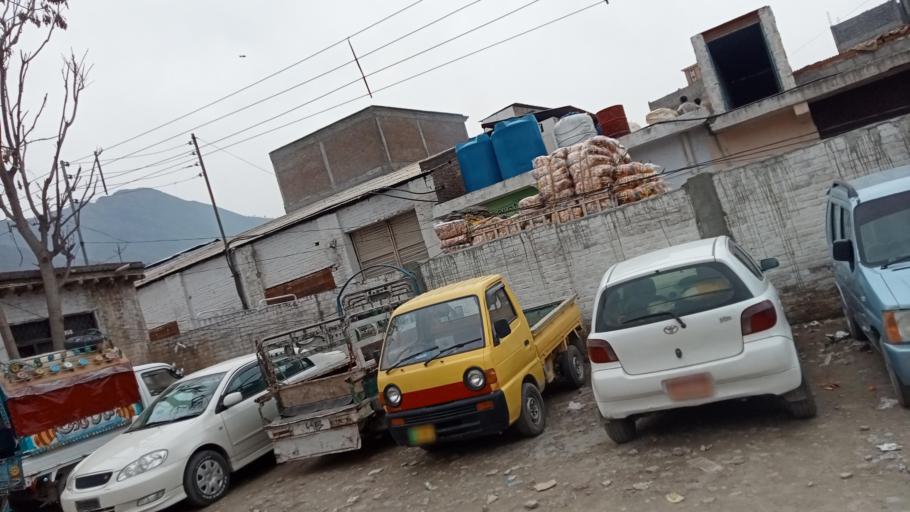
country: PK
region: Khyber Pakhtunkhwa
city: Mingora
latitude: 34.7693
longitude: 72.3405
